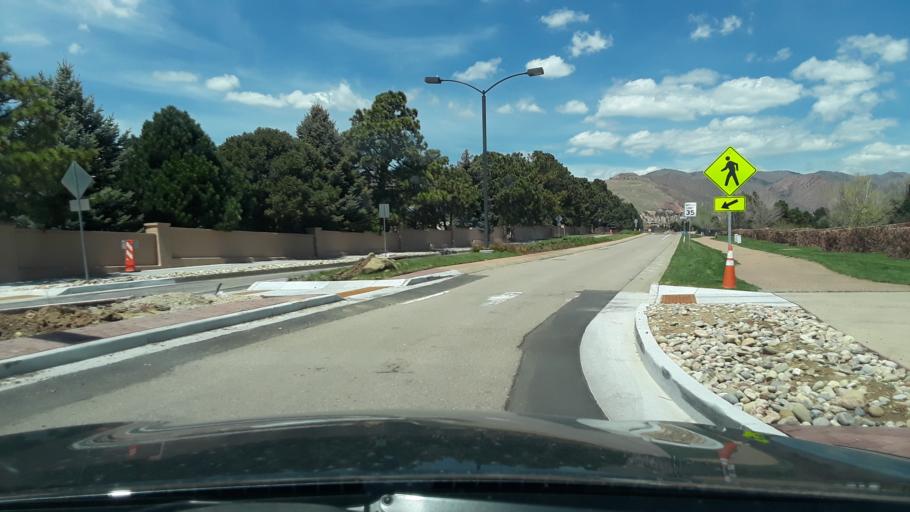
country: US
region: Colorado
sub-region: El Paso County
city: Manitou Springs
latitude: 38.8782
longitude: -104.8660
